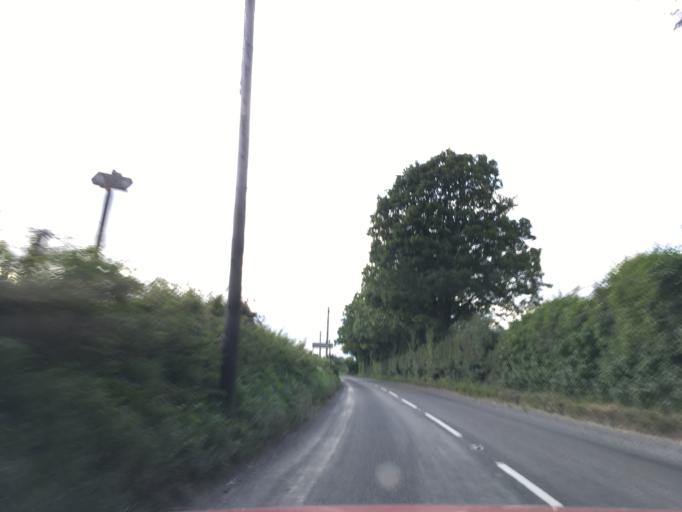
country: GB
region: England
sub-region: Wiltshire
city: Market Lavington
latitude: 51.3167
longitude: -1.9176
